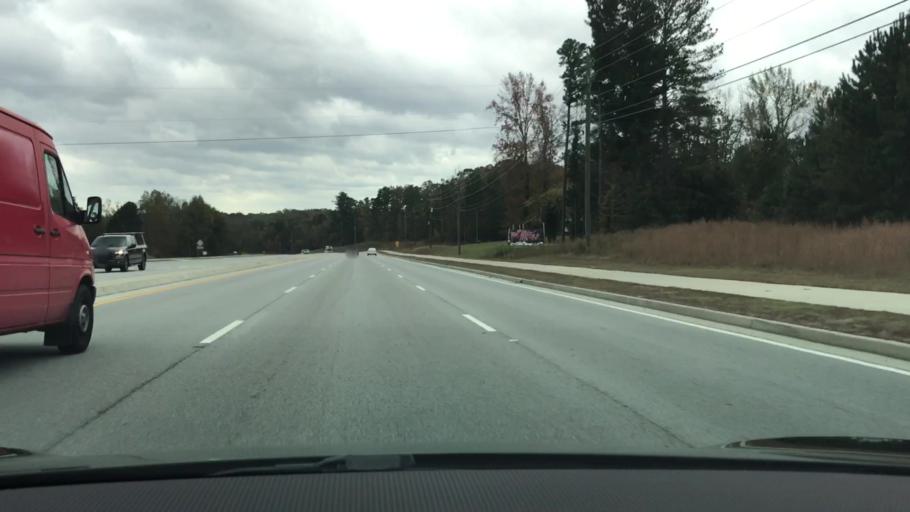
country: US
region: Georgia
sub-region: Hall County
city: Flowery Branch
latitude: 34.1262
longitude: -83.9217
